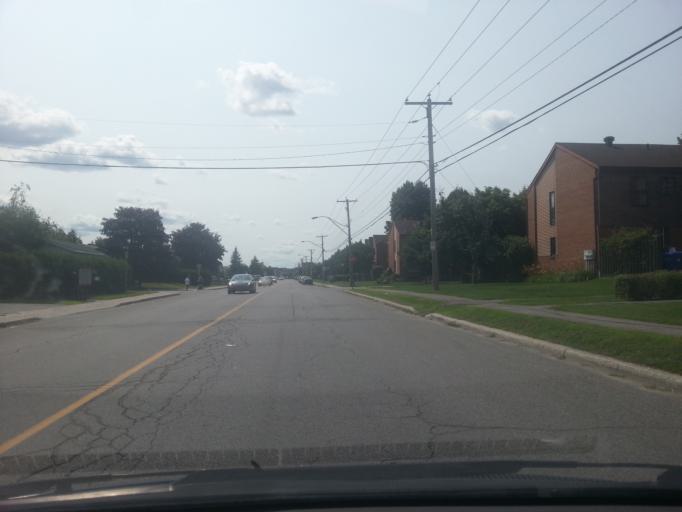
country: CA
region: Quebec
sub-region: Outaouais
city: Gatineau
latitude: 45.4890
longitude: -75.6969
